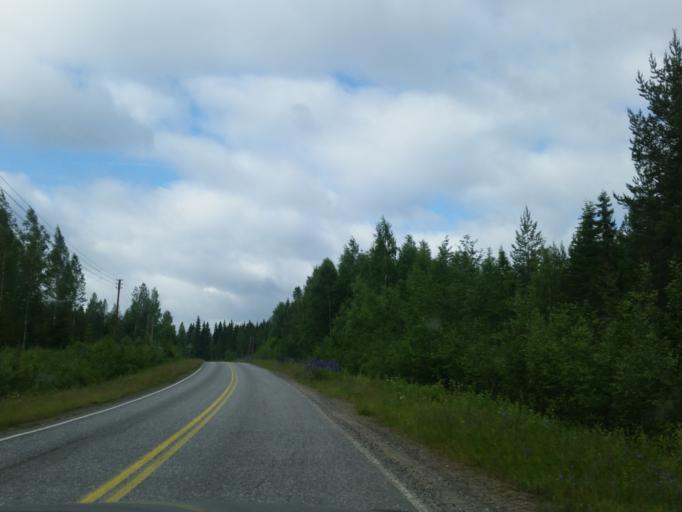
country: FI
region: Northern Savo
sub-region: Sisae-Savo
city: Tervo
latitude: 63.0277
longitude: 26.6907
